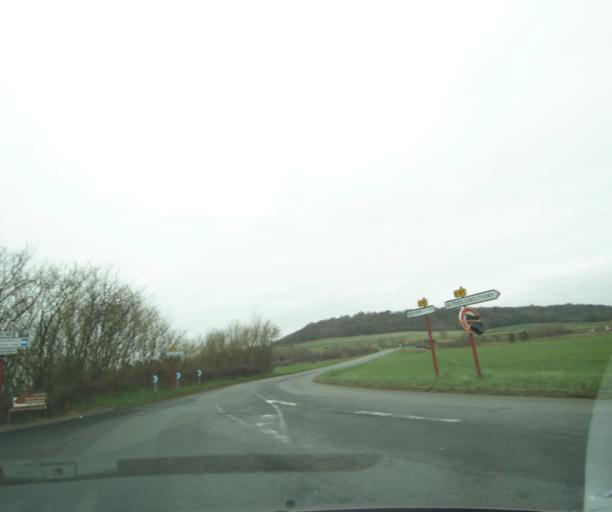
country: FR
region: Picardie
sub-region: Departement de l'Oise
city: Noyon
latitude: 49.5756
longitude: 3.0327
